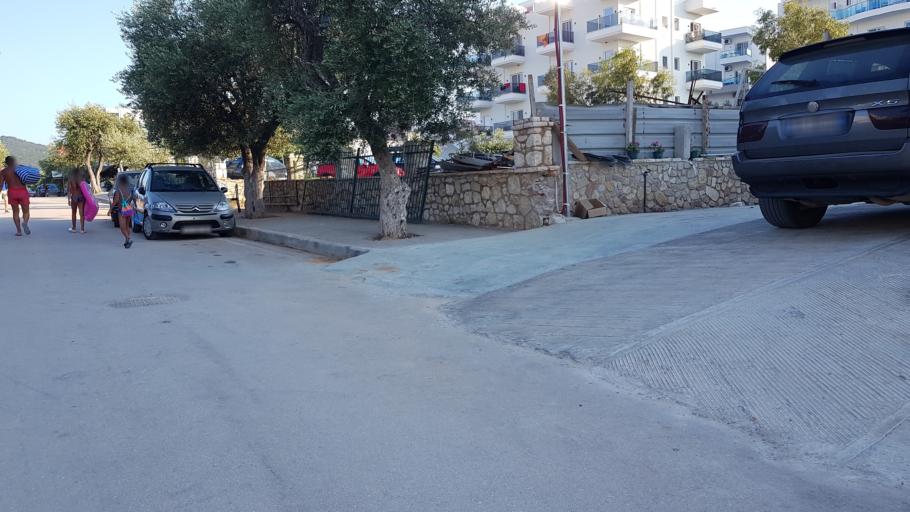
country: AL
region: Vlore
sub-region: Rrethi i Sarandes
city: Xarre
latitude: 39.7722
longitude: 20.0023
